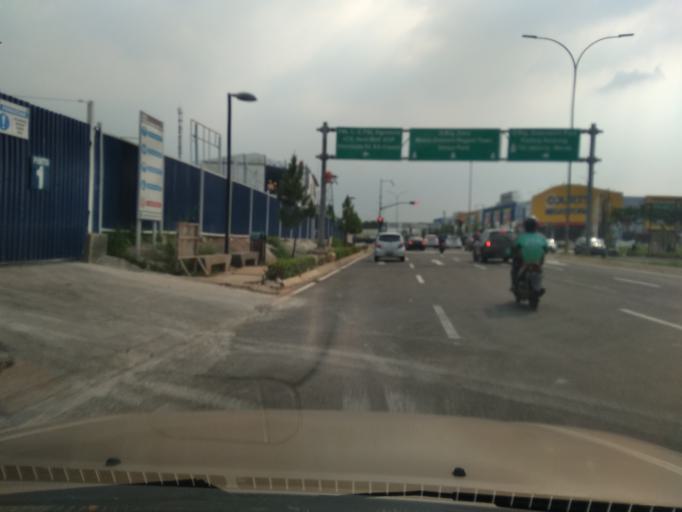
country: ID
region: West Java
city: Serpong
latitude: -6.2871
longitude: 106.6400
